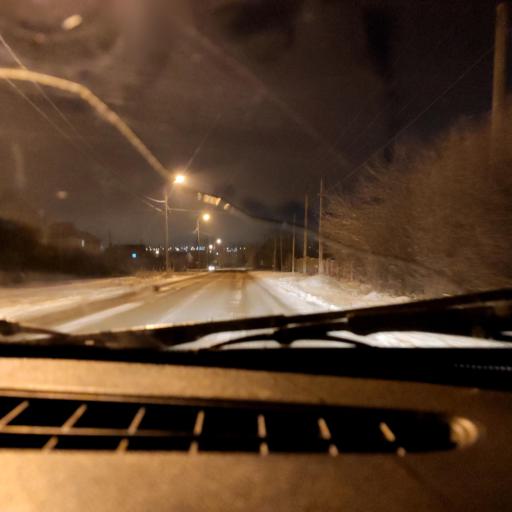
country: RU
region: Bashkortostan
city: Ufa
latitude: 54.6029
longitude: 55.9484
